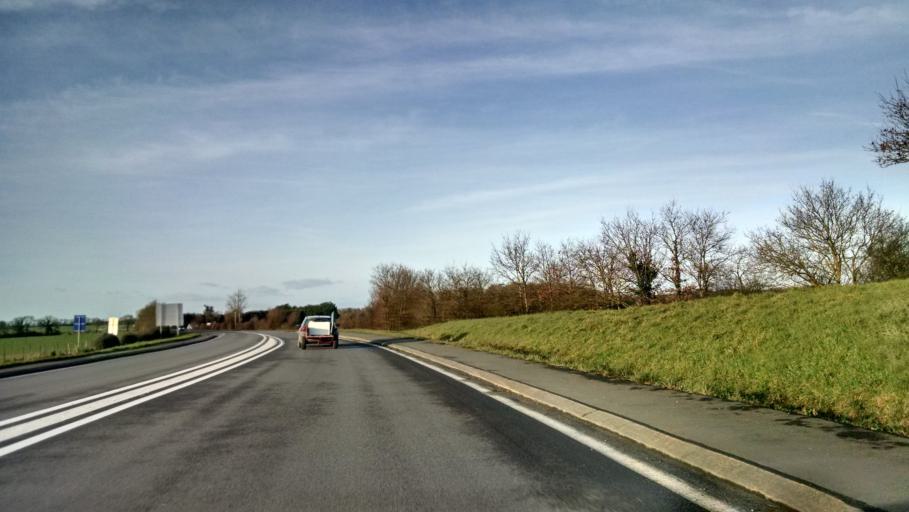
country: FR
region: Pays de la Loire
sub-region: Departement de la Vendee
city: Saint-Hilaire-de-Loulay
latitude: 47.0102
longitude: -1.3382
